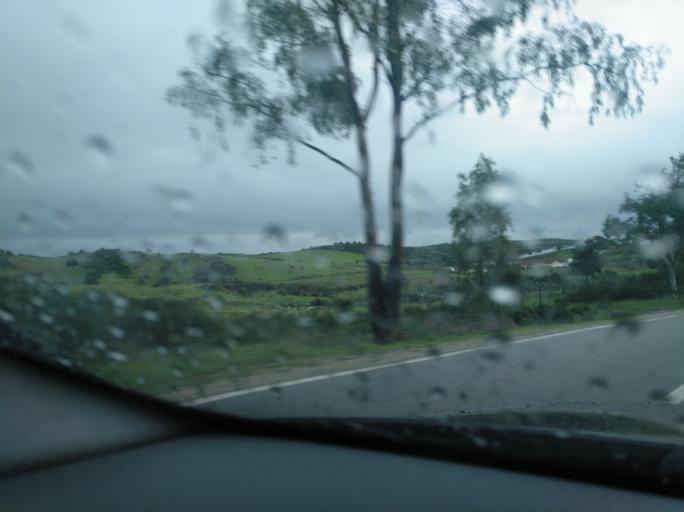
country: PT
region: Beja
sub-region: Mertola
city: Mertola
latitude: 37.5858
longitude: -7.6867
